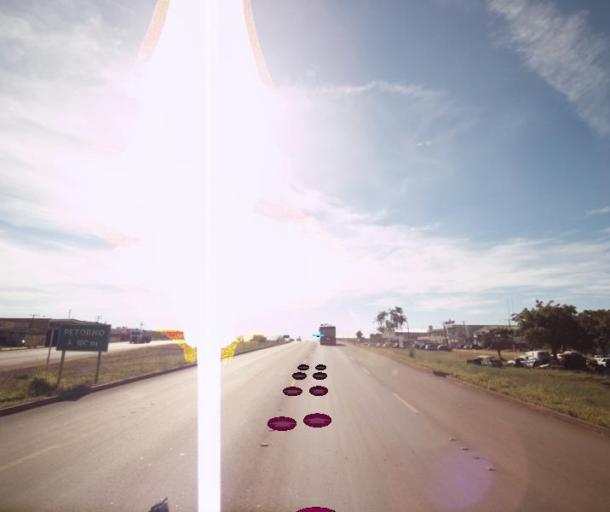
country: BR
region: Federal District
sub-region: Brasilia
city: Brasilia
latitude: -15.7375
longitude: -48.2921
